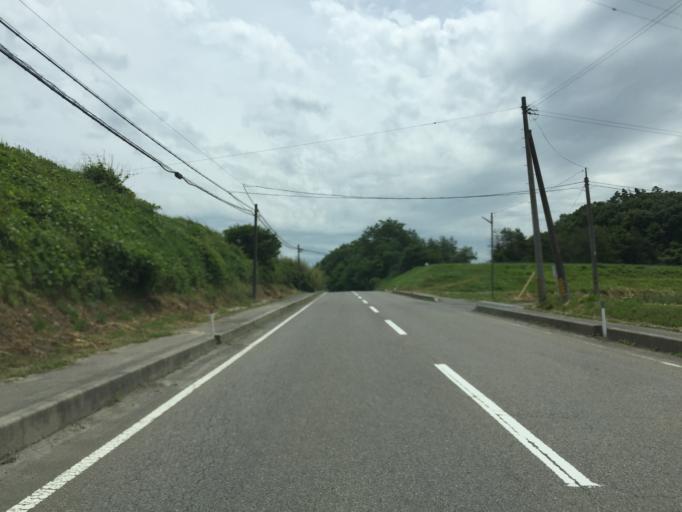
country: JP
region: Fukushima
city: Miharu
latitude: 37.4292
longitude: 140.4986
